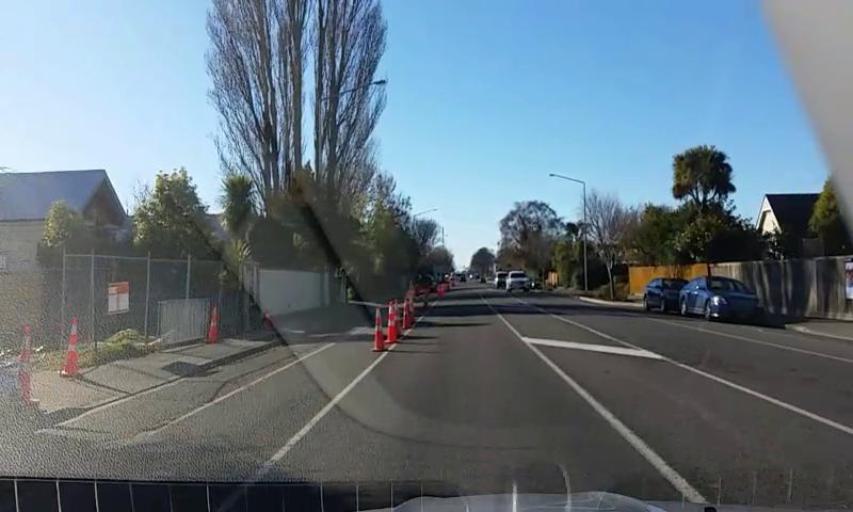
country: NZ
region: Canterbury
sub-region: Christchurch City
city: Christchurch
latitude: -43.5081
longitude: 172.6479
